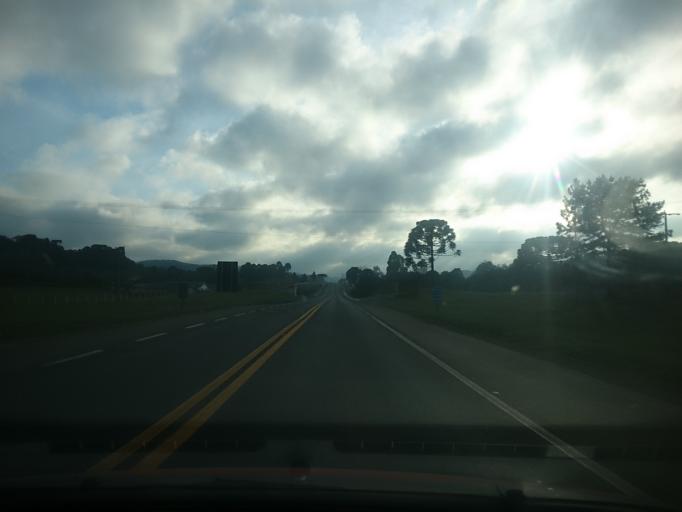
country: BR
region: Santa Catarina
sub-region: Lages
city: Lages
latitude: -28.0092
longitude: -50.5443
